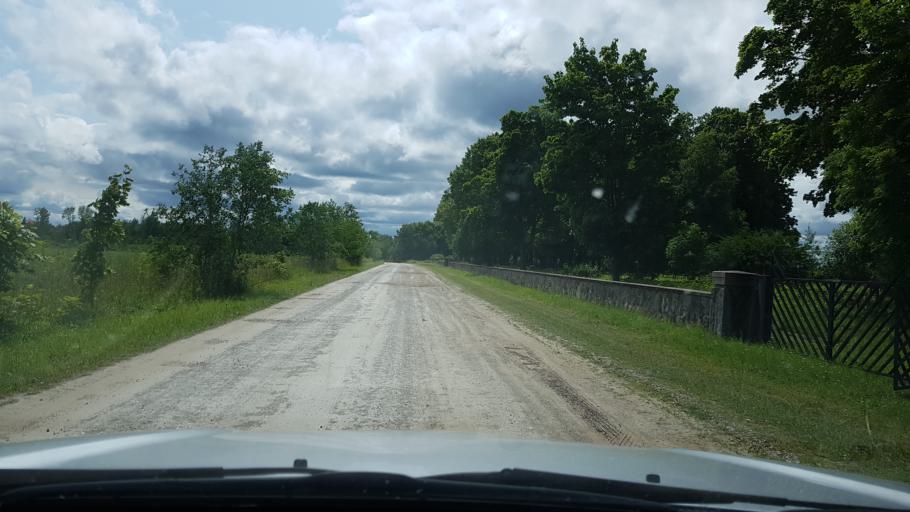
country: EE
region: Ida-Virumaa
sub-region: Sillamaee linn
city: Sillamae
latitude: 59.3707
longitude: 27.8469
